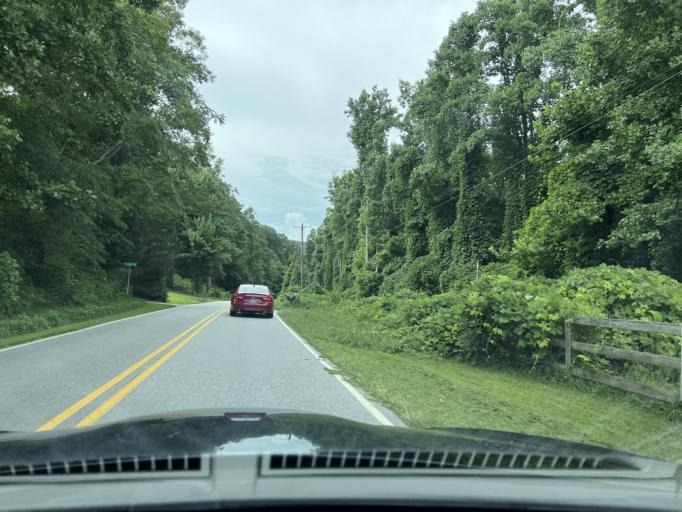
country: US
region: North Carolina
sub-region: Henderson County
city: Fruitland
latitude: 35.4091
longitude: -82.4097
